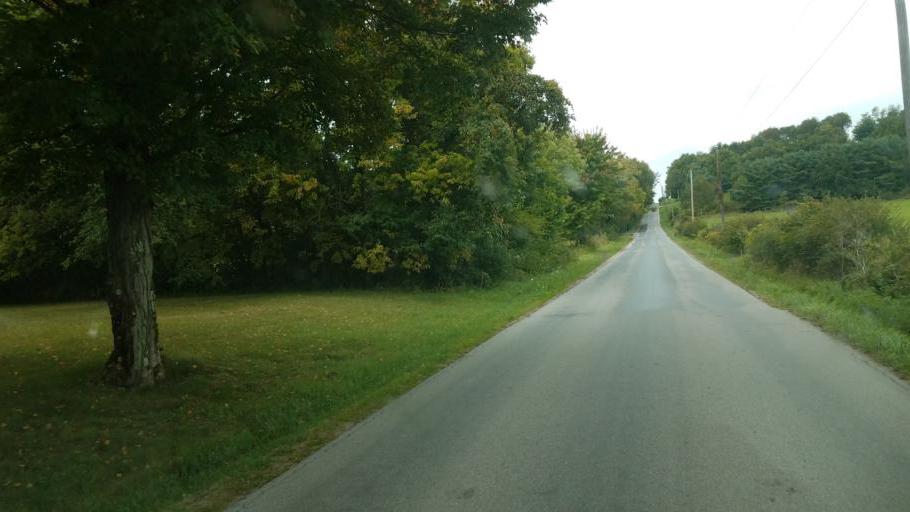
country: US
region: Ohio
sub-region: Knox County
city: Centerburg
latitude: 40.3213
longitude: -82.7199
